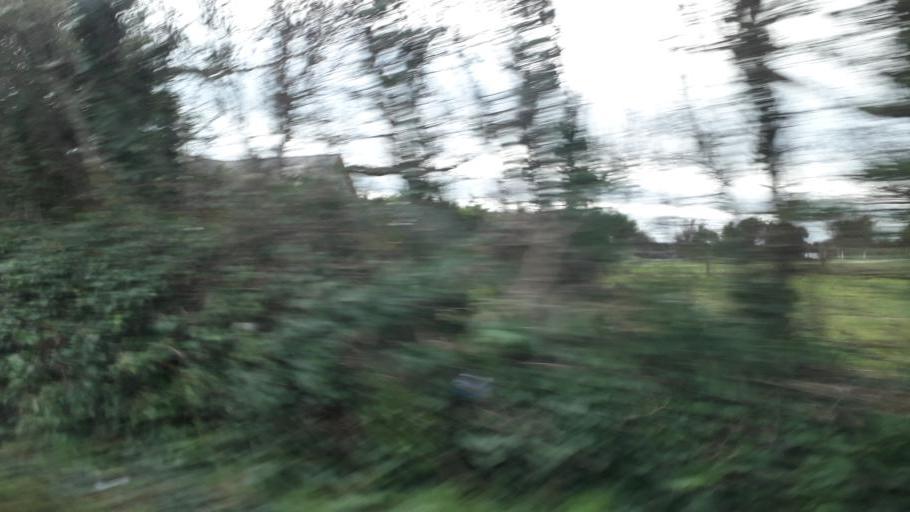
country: IE
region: Leinster
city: An Ros
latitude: 53.5438
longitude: -6.0978
